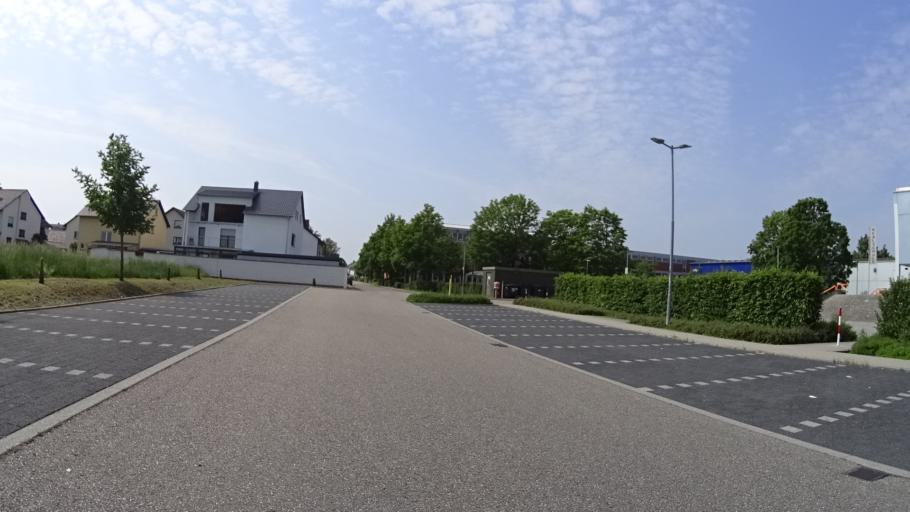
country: DE
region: Baden-Wuerttemberg
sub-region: Karlsruhe Region
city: Linkenheim-Hochstetten
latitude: 49.1278
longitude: 8.4159
